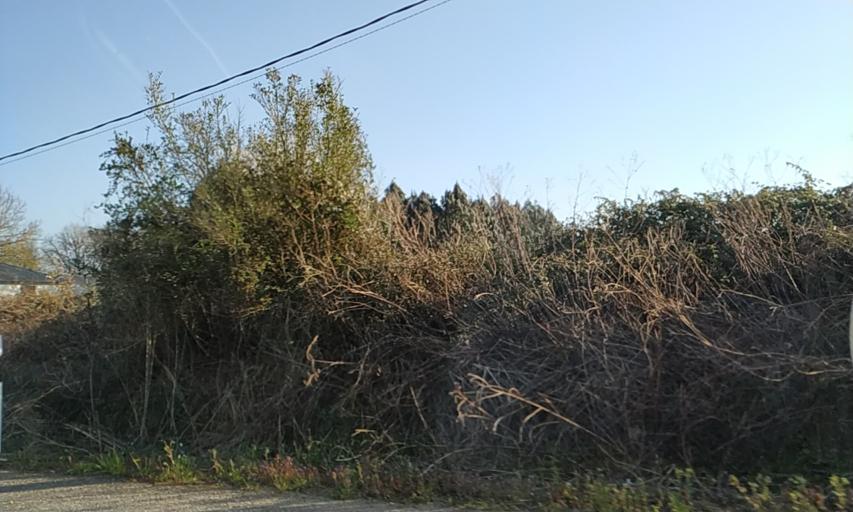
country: ES
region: Galicia
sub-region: Provincia de Lugo
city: Corgo
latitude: 42.9502
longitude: -7.4539
